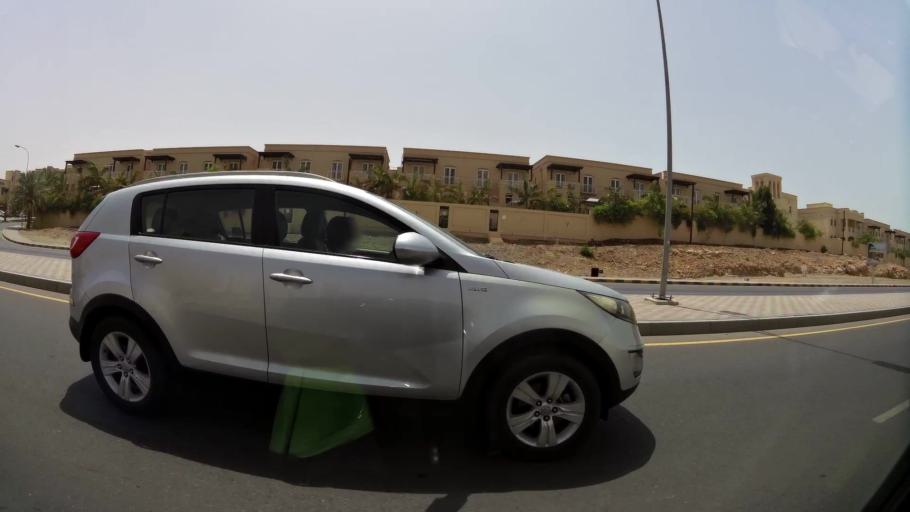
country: OM
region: Muhafazat Masqat
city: Bawshar
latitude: 23.5591
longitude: 58.4020
